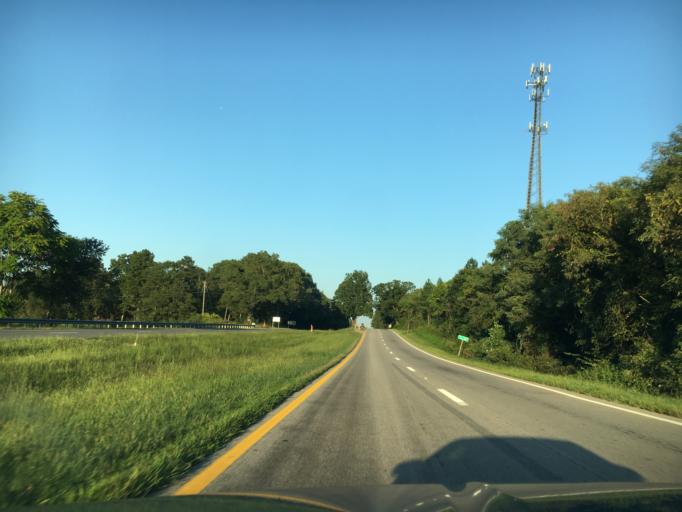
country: US
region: Virginia
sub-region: Halifax County
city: Mountain Road
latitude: 36.5846
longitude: -79.1389
